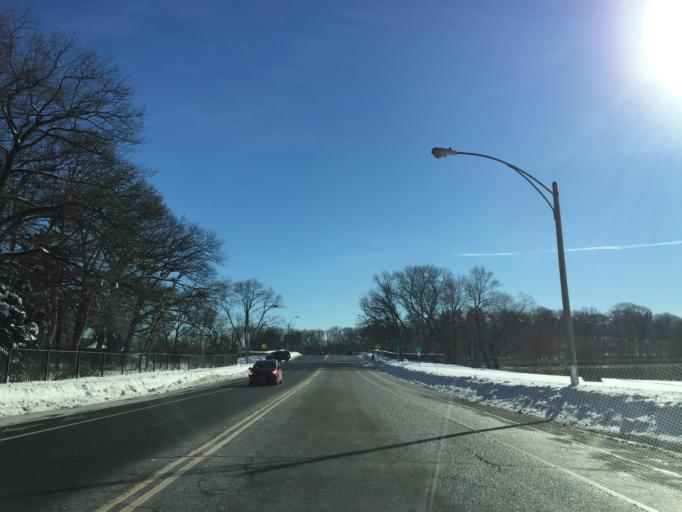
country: US
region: Massachusetts
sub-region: Middlesex County
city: Watertown
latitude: 42.3599
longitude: -71.1634
